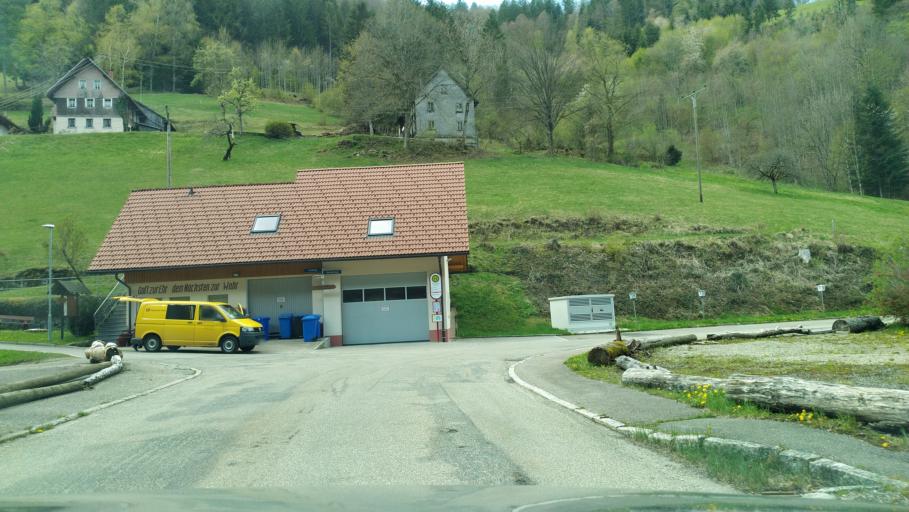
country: DE
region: Baden-Wuerttemberg
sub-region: Freiburg Region
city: Sankt Margen
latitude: 48.0312
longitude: 8.1158
